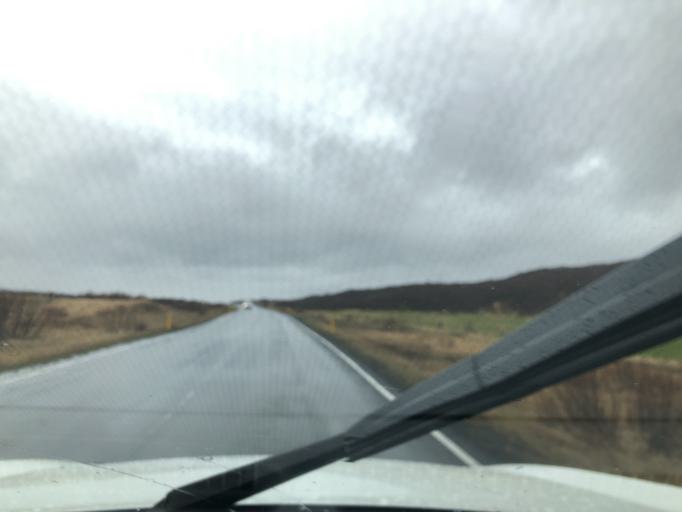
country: IS
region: South
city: Selfoss
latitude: 64.2319
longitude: -20.5644
